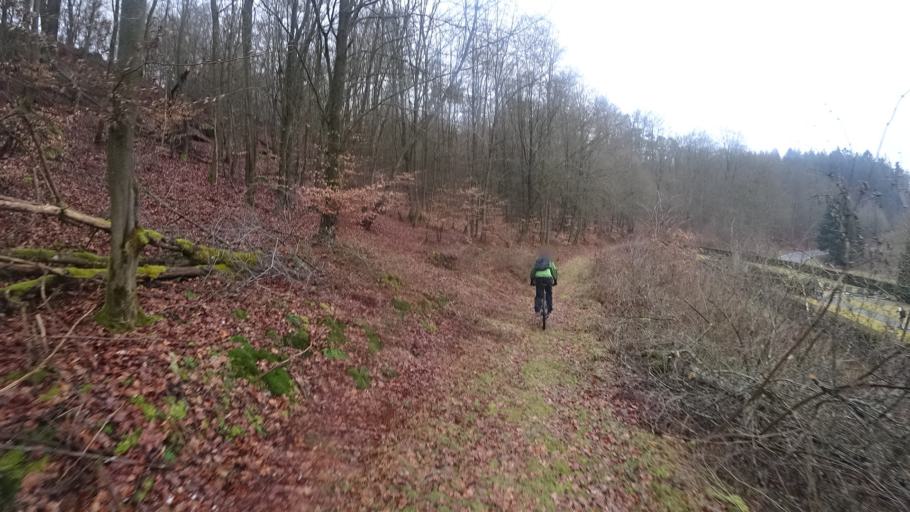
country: DE
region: Rheinland-Pfalz
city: Welterod
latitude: 50.1411
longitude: 7.8808
